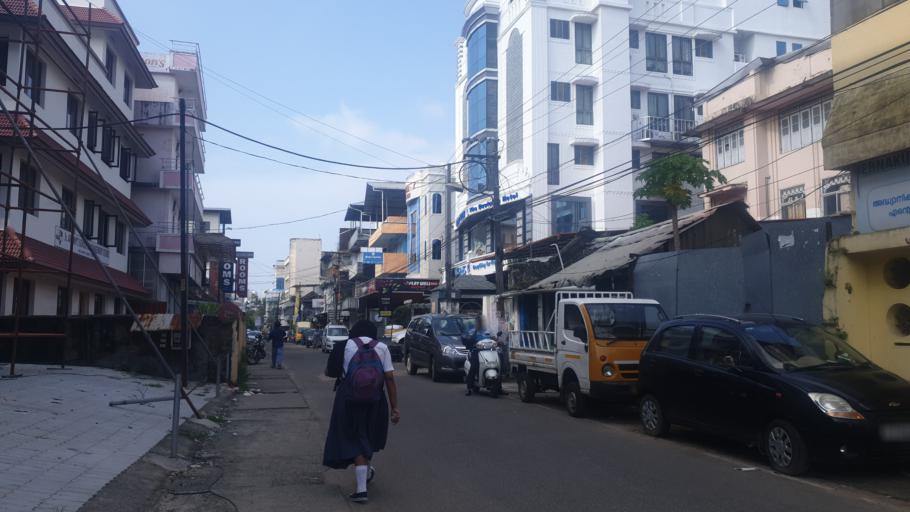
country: IN
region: Kerala
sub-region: Ernakulam
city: Cochin
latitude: 9.9834
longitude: 76.2775
